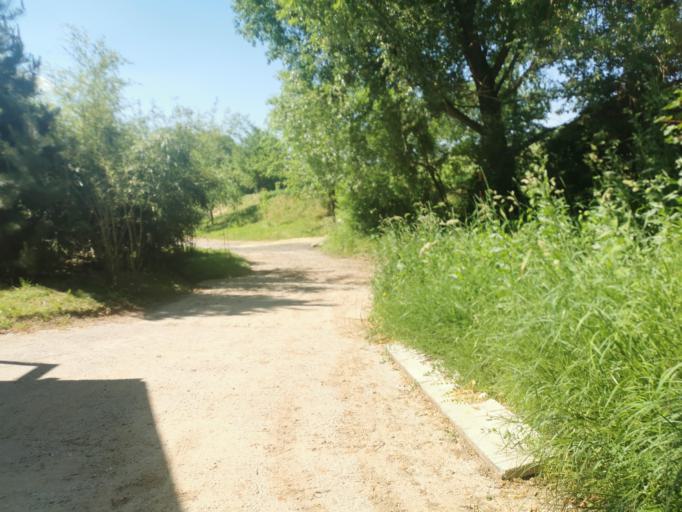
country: SK
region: Trnavsky
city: Smolenice
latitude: 48.5533
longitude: 17.3558
